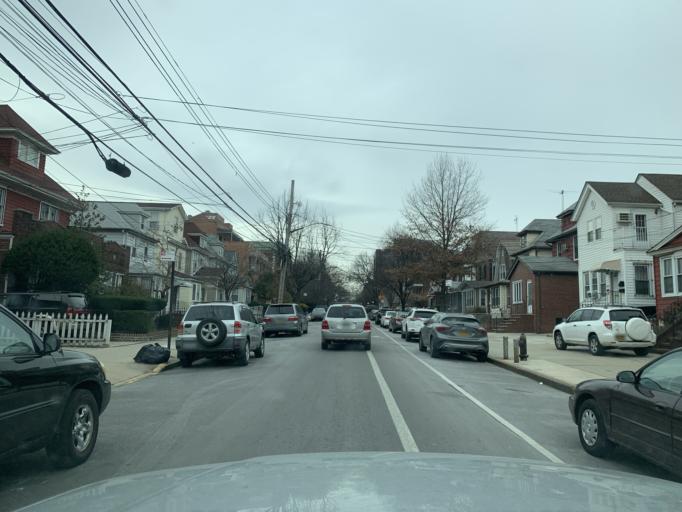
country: US
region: New York
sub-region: Queens County
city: Borough of Queens
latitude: 40.7373
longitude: -73.8710
